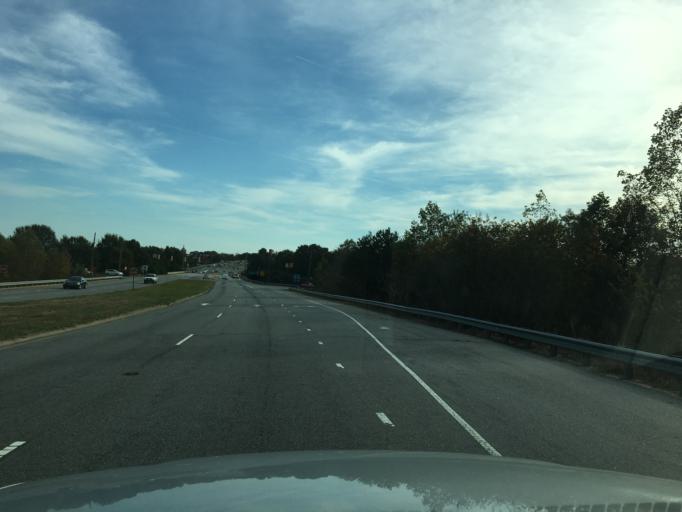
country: US
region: North Carolina
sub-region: Catawba County
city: Hickory
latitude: 35.7109
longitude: -81.2952
